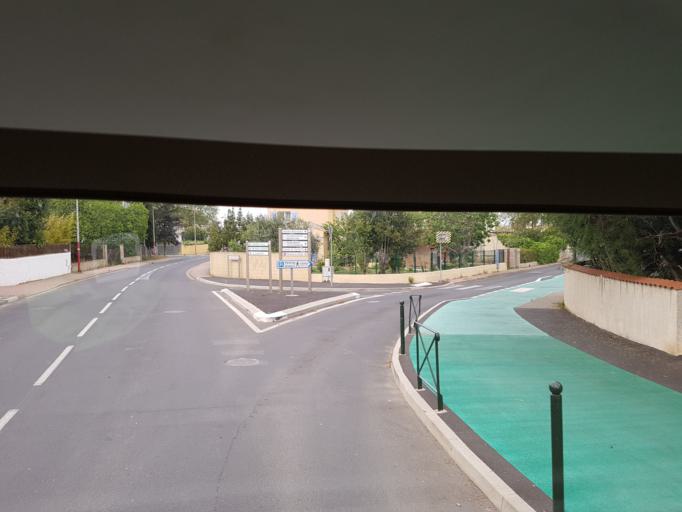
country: FR
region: Languedoc-Roussillon
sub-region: Departement de l'Herault
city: Serignan
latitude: 43.2783
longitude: 3.2736
